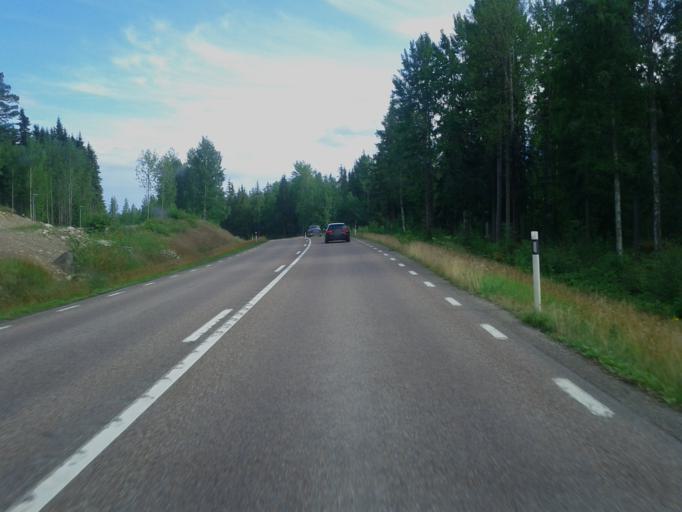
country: SE
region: Dalarna
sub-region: Faluns Kommun
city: Grycksbo
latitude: 60.6748
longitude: 15.5115
